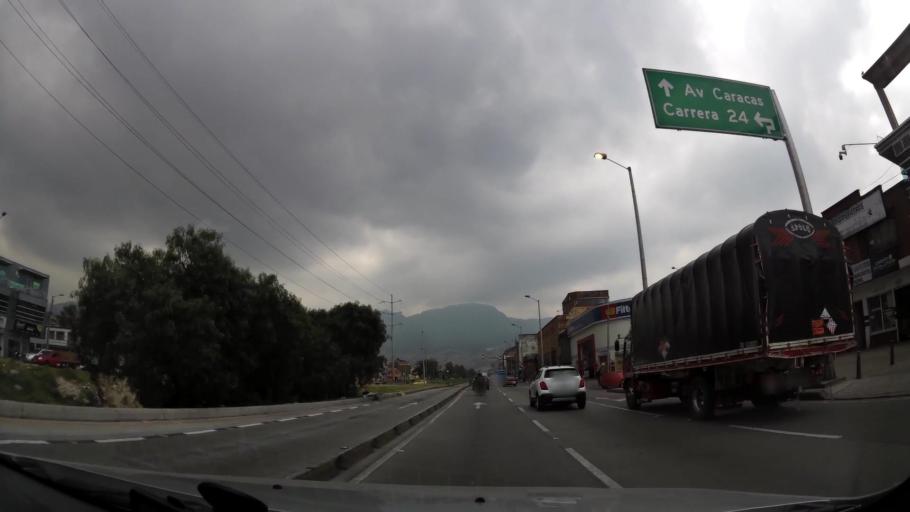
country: CO
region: Bogota D.C.
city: Bogota
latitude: 4.6034
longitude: -74.0940
